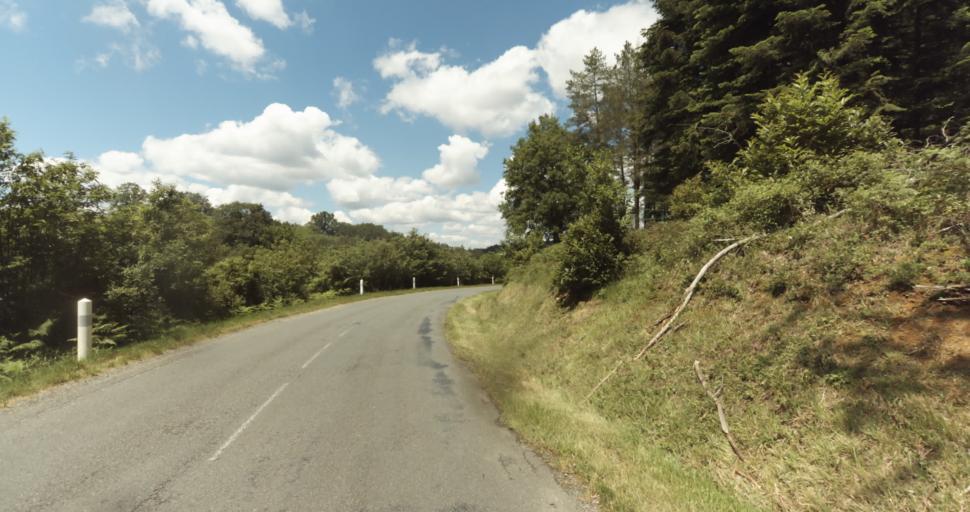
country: FR
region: Aquitaine
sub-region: Departement de la Dordogne
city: Beaumont-du-Perigord
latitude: 44.8093
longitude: 0.8566
